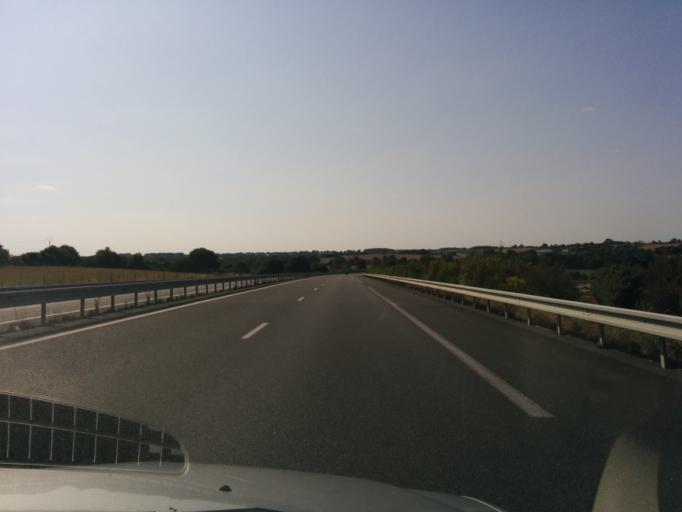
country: FR
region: Poitou-Charentes
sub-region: Departement des Deux-Sevres
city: Combrand
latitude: 46.9060
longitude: -0.6742
